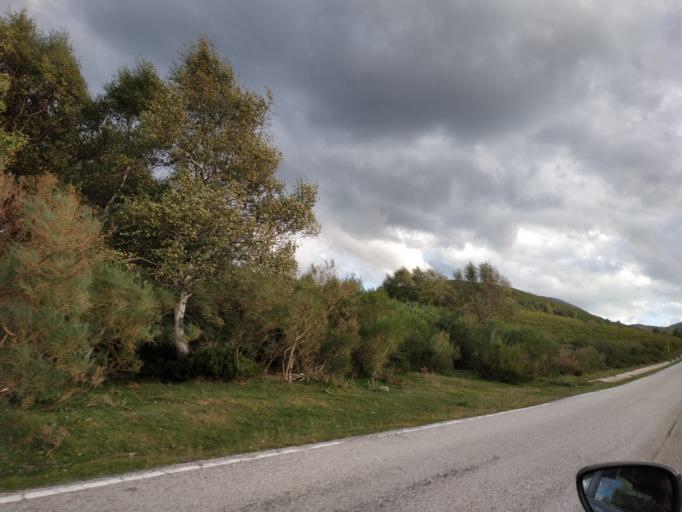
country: ES
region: Castille and Leon
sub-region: Provincia de Leon
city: Candin
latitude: 42.8793
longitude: -6.8281
